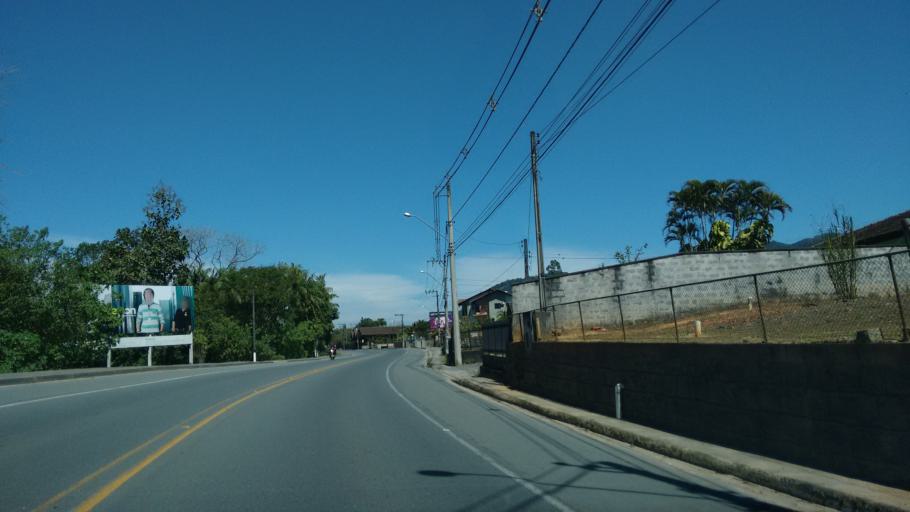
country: BR
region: Santa Catarina
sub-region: Pomerode
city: Pomerode
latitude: -26.7572
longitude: -49.1716
